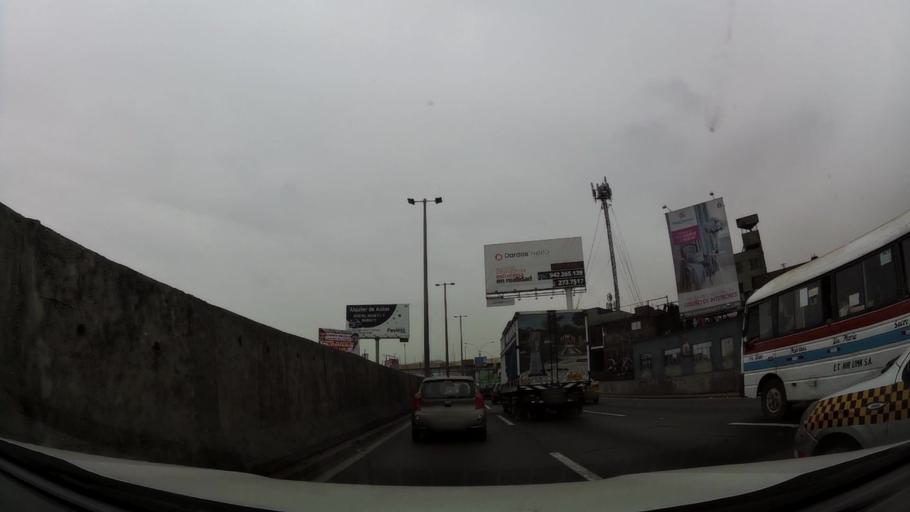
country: PE
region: Lima
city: Lima
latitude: -12.0317
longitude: -77.0558
